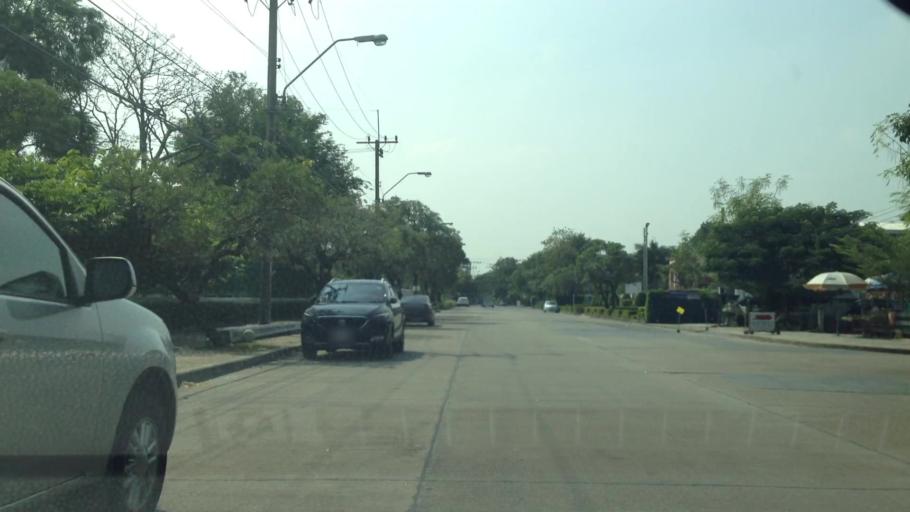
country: TH
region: Bangkok
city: Bang Na
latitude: 13.6876
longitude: 100.6579
